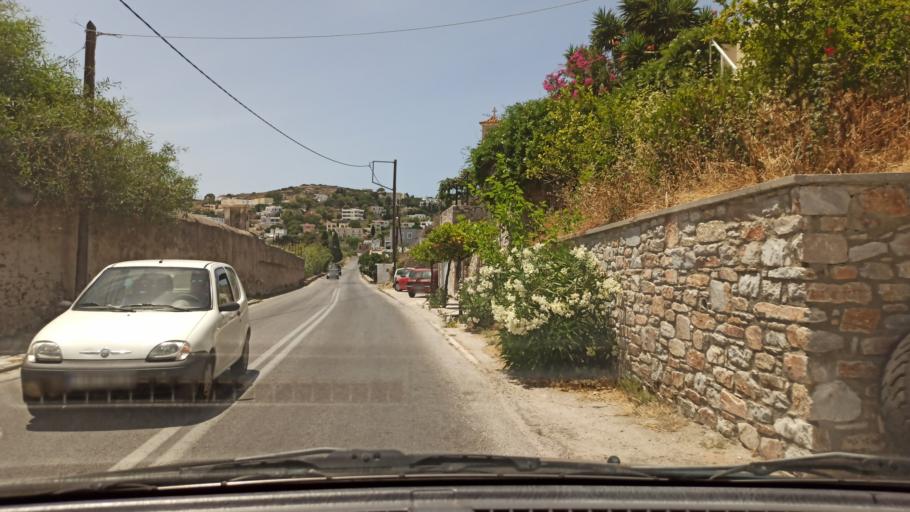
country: GR
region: South Aegean
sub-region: Nomos Kykladon
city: Ermoupolis
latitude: 37.4301
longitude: 24.9333
